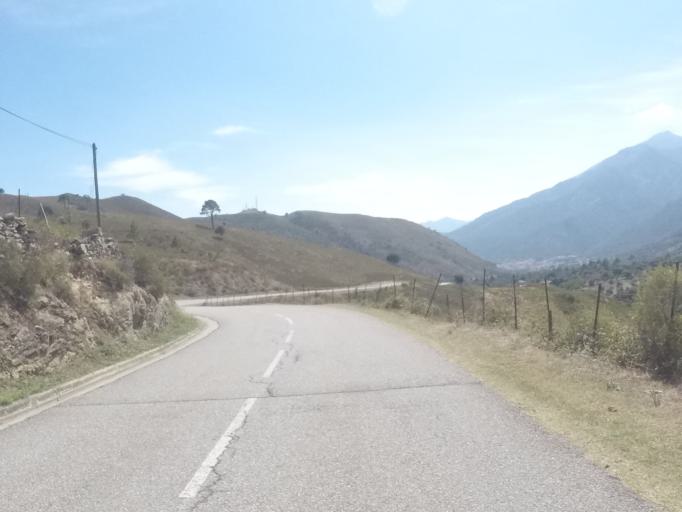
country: FR
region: Corsica
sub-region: Departement de la Haute-Corse
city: Corte
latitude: 42.3426
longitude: 9.1487
